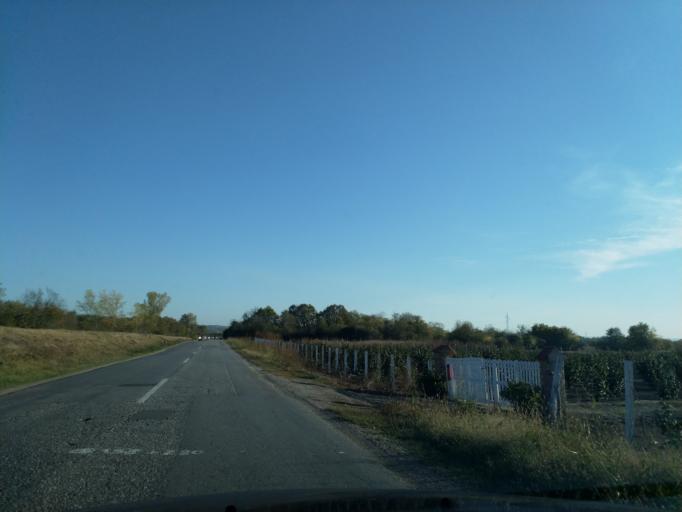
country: RS
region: Central Serbia
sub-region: Pomoravski Okrug
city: Svilajnac
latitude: 44.2278
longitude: 21.1459
